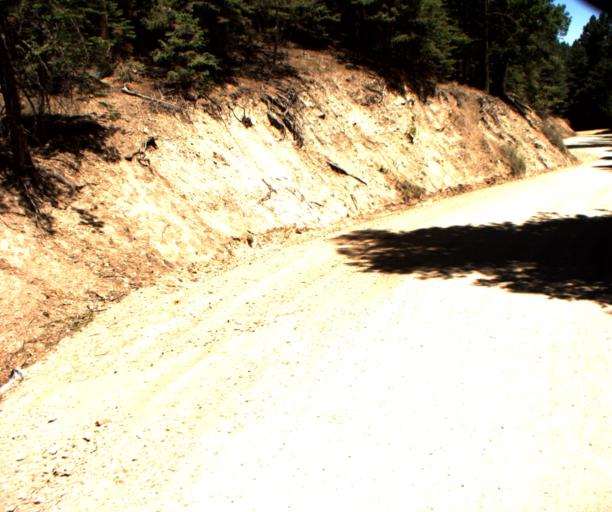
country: US
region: Arizona
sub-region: Graham County
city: Swift Trail Junction
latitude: 32.6836
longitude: -109.8967
